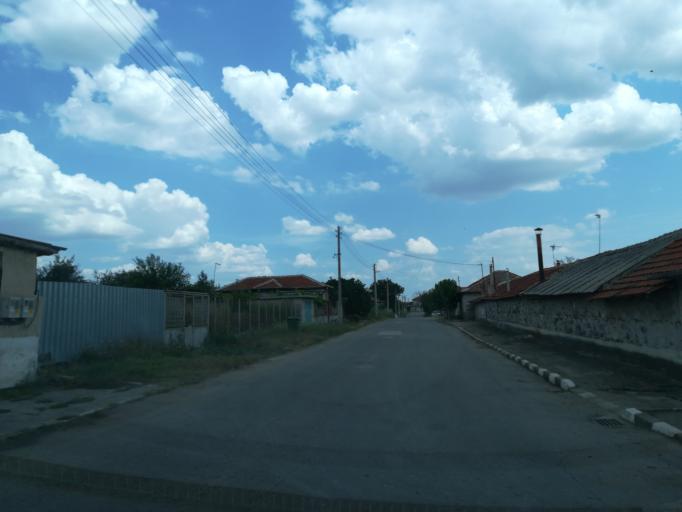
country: BG
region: Khaskovo
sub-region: Obshtina Mineralni Bani
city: Mineralni Bani
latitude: 41.9829
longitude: 25.1683
